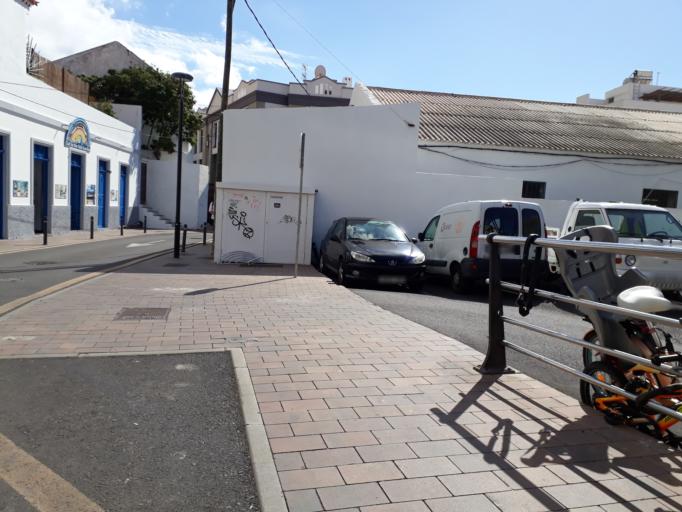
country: ES
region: Canary Islands
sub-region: Provincia de Santa Cruz de Tenerife
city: Alajero
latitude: 28.0830
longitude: -17.3337
